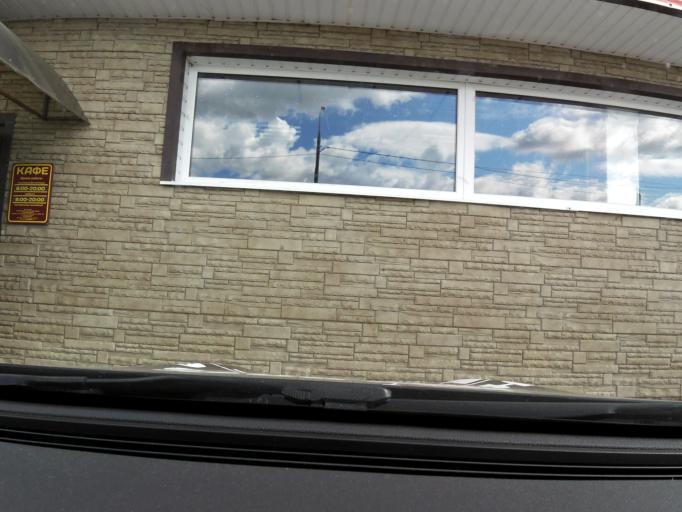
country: RU
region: Tverskaya
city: Likhoslavl'
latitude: 56.9778
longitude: 35.2679
